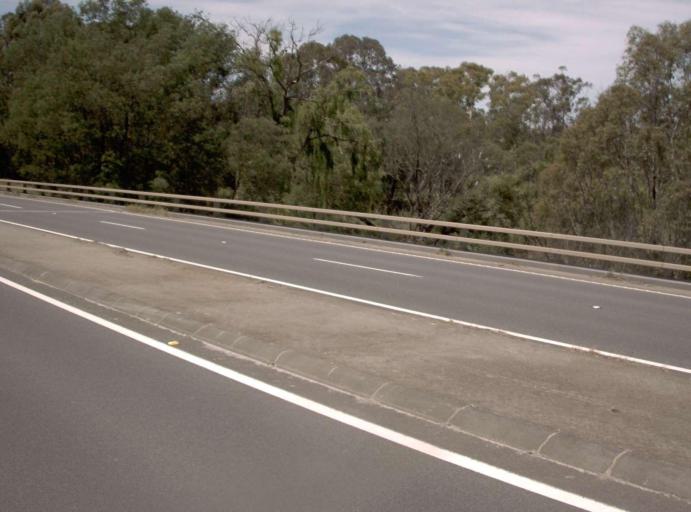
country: AU
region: Victoria
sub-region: Wellington
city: Heyfield
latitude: -38.1427
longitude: 146.7923
